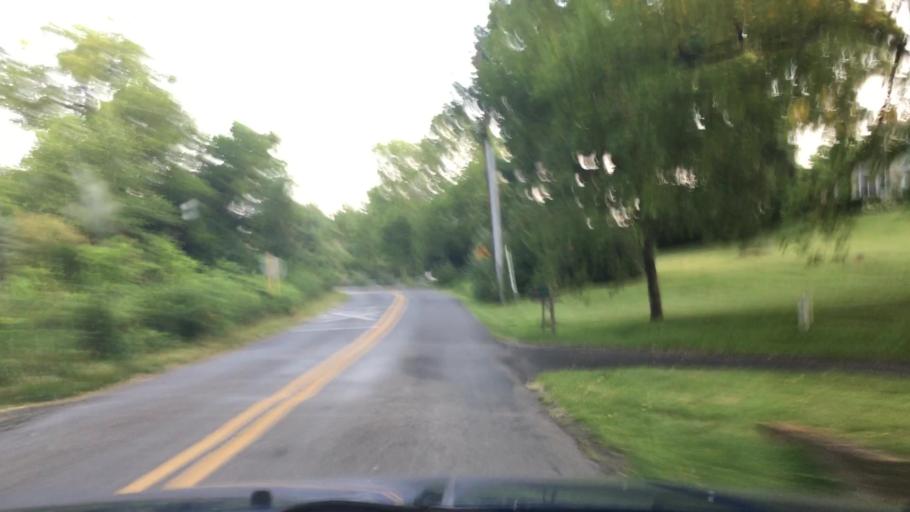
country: US
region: Virginia
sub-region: Augusta County
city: Verona
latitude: 38.2393
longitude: -78.9699
